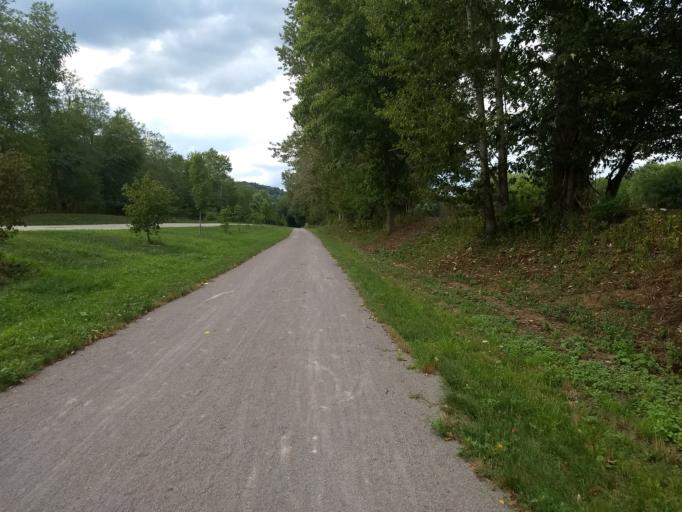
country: US
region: Pennsylvania
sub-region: Armstrong County
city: Freeport
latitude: 40.6582
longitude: -79.6902
